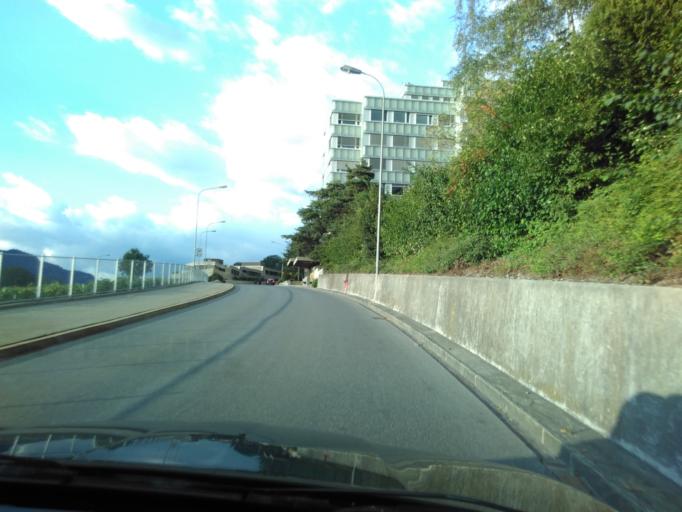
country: CH
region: Grisons
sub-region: Plessur District
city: Chur
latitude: 46.8603
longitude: 9.5410
